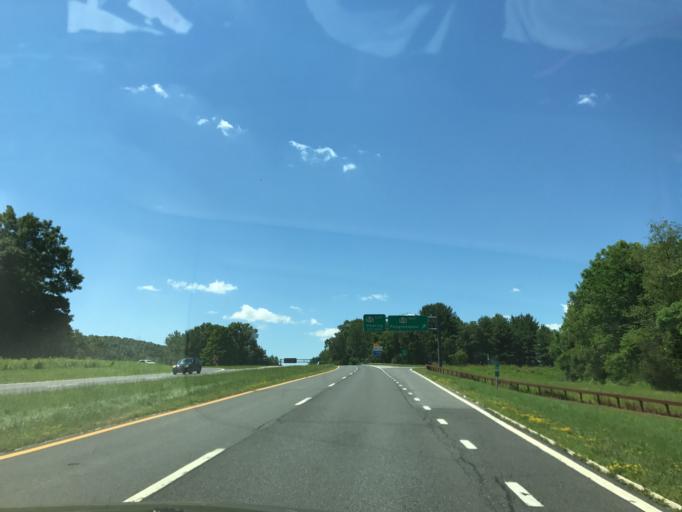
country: US
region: New York
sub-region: Dutchess County
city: Hillside Lake
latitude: 41.6733
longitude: -73.7878
